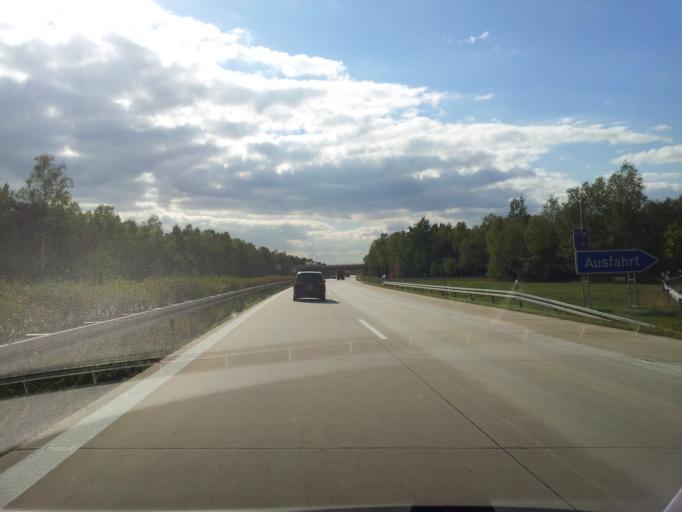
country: DE
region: Brandenburg
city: Schipkau
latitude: 51.4925
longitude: 13.8946
